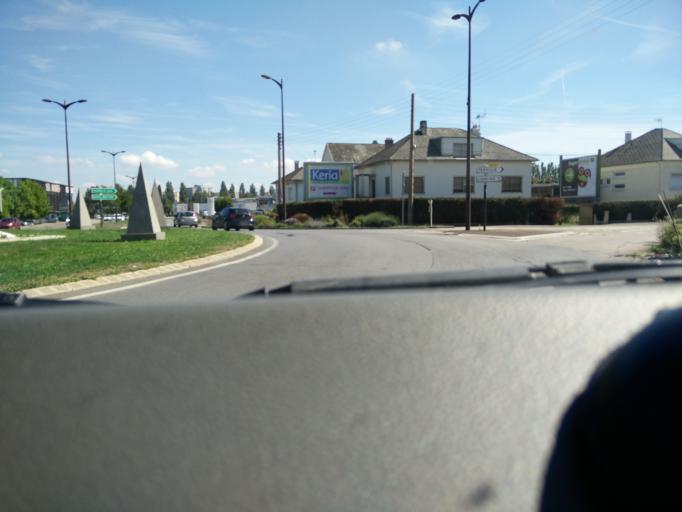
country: FR
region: Lorraine
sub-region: Departement de la Moselle
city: Terville
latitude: 49.3576
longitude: 6.1366
